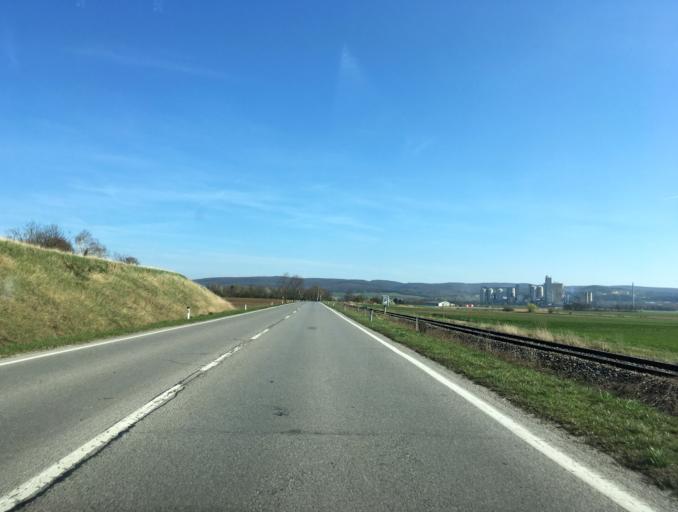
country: AT
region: Lower Austria
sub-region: Politischer Bezirk Bruck an der Leitha
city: Gotzendorf an der Leitha
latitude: 48.0037
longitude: 16.5920
